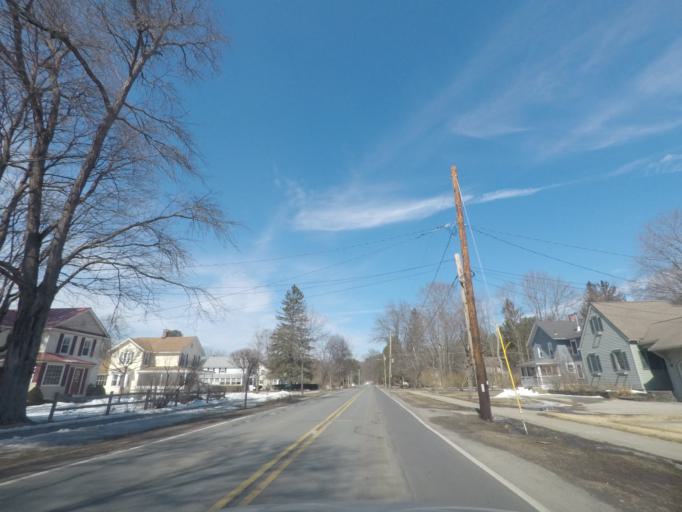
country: US
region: Massachusetts
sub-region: Berkshire County
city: Stockbridge
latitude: 42.2895
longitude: -73.3209
